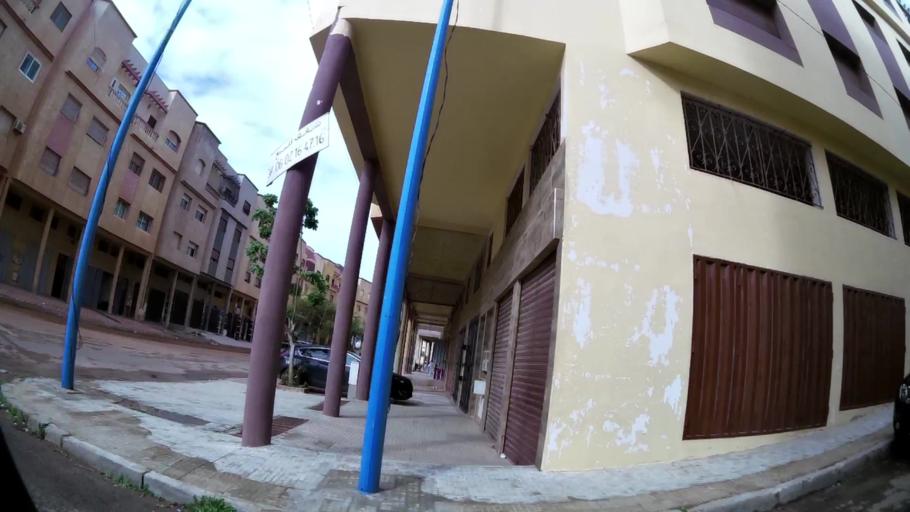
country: MA
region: Grand Casablanca
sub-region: Mohammedia
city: Mohammedia
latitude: 33.6857
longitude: -7.3711
